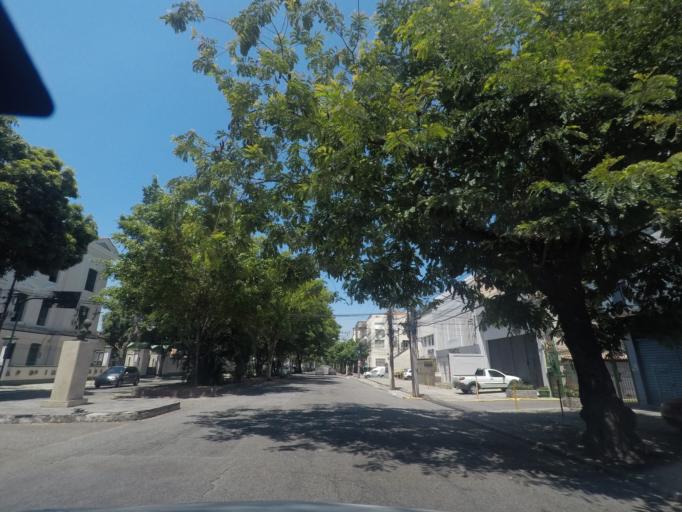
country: BR
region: Rio de Janeiro
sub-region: Rio De Janeiro
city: Rio de Janeiro
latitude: -22.9033
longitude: -43.2142
